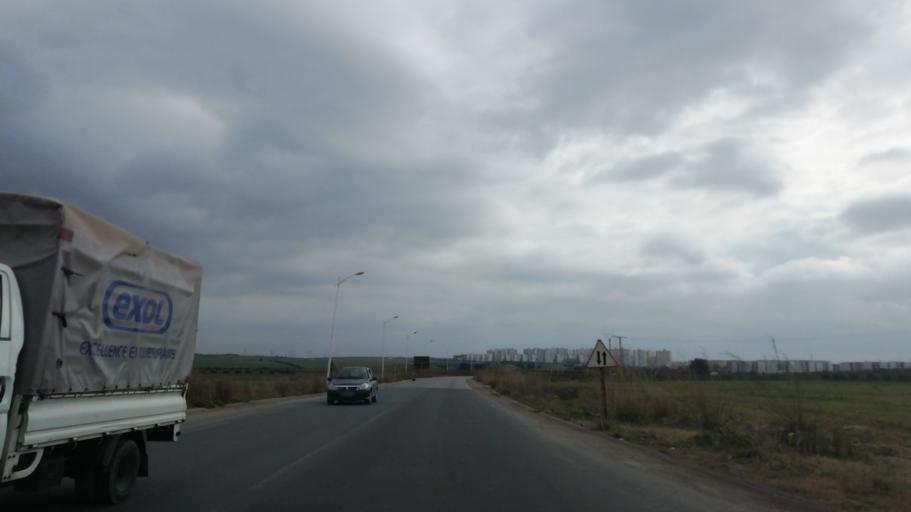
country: DZ
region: Oran
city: Sidi ech Chahmi
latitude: 35.5670
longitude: -0.4493
